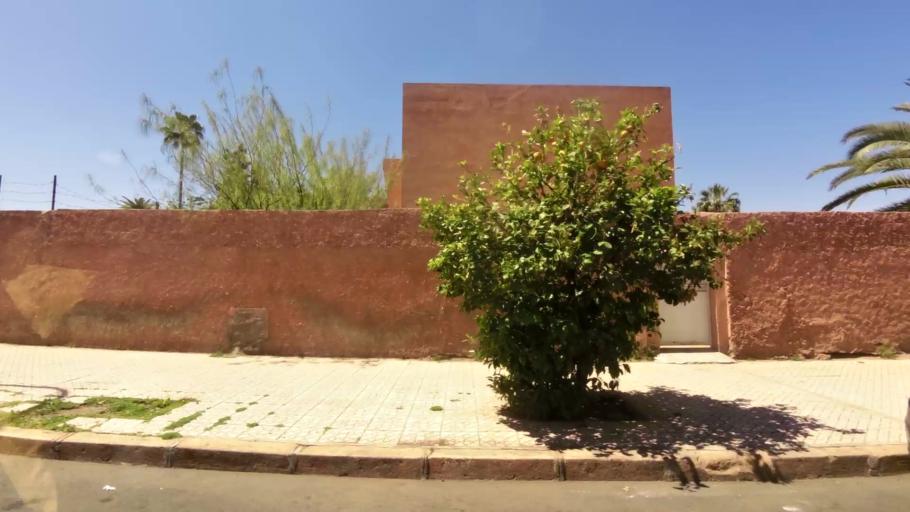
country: MA
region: Marrakech-Tensift-Al Haouz
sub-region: Marrakech
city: Marrakesh
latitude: 31.6292
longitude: -8.0051
